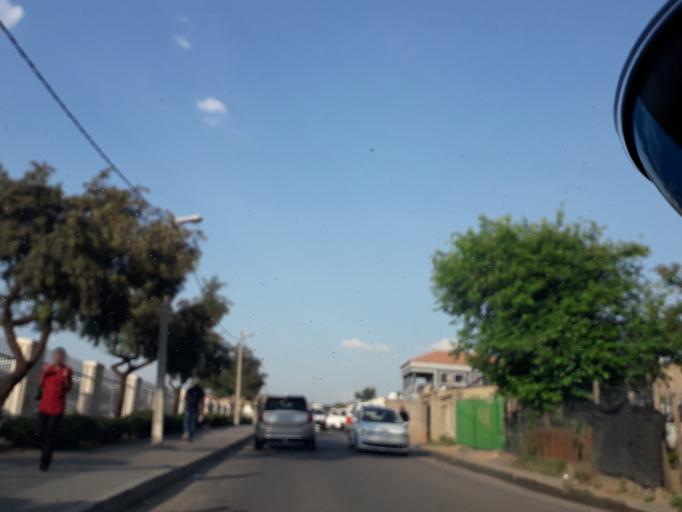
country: ZA
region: Gauteng
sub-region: City of Johannesburg Metropolitan Municipality
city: Modderfontein
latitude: -26.0847
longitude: 28.1111
